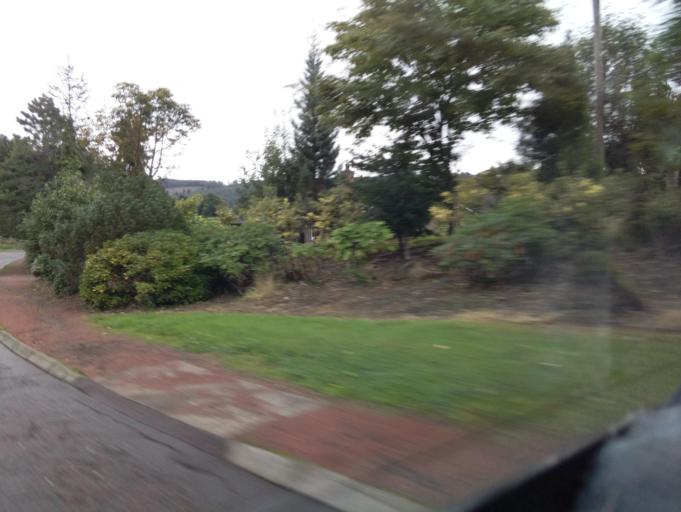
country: GB
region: Scotland
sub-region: Clackmannanshire
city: Tillicoultry
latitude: 56.1555
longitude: -3.7290
